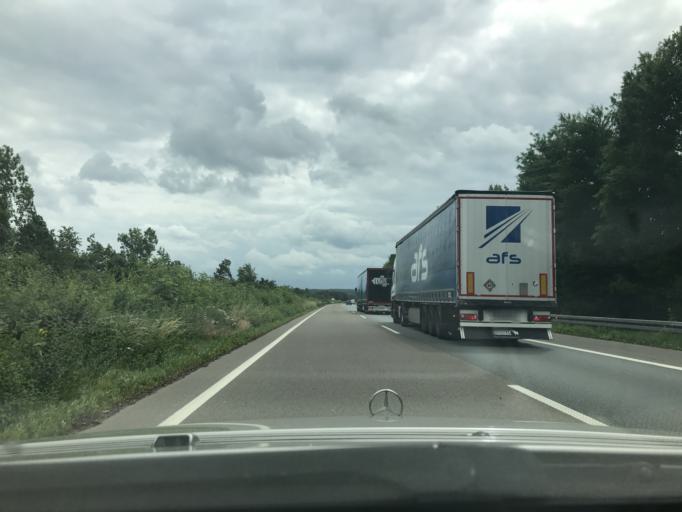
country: DE
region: North Rhine-Westphalia
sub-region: Regierungsbezirk Arnsberg
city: Werl
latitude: 51.5553
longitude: 7.8904
